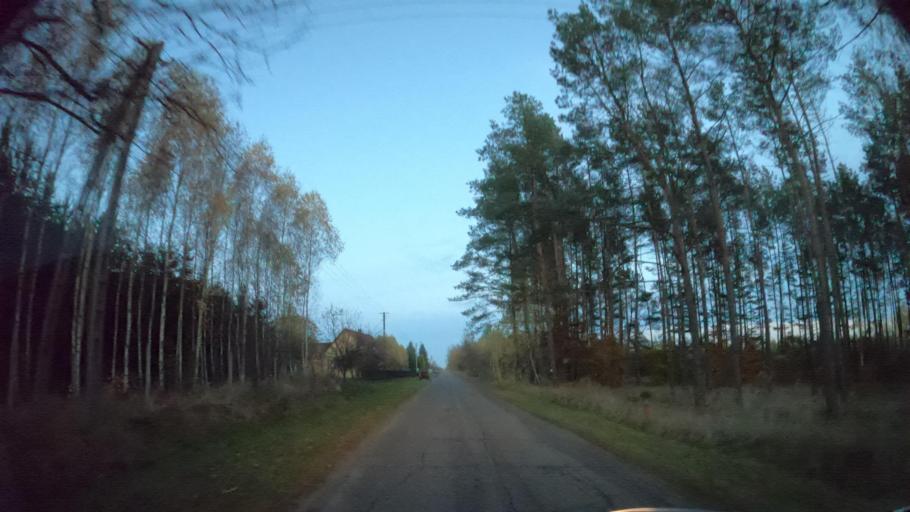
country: PL
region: Greater Poland Voivodeship
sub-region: Powiat zlotowski
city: Sypniewo
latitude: 53.4266
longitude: 16.6038
